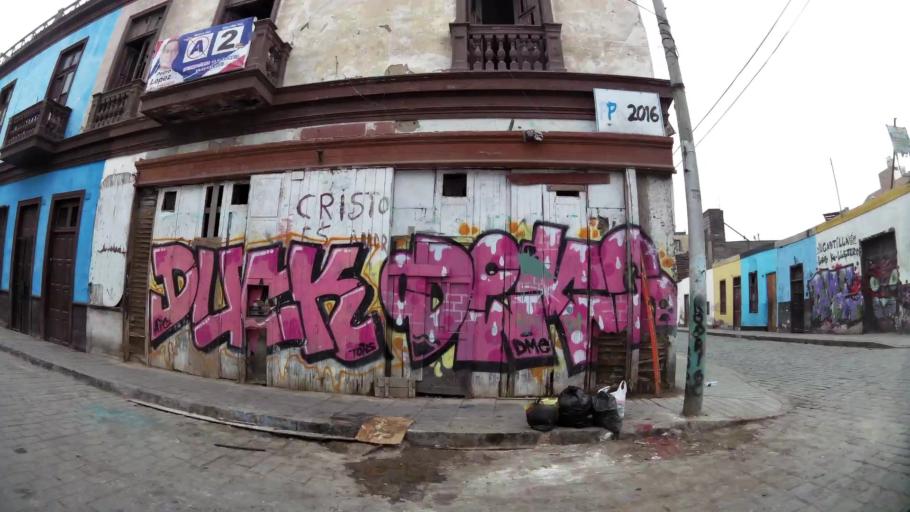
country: PE
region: Callao
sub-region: Callao
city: Callao
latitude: -12.0584
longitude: -77.1447
